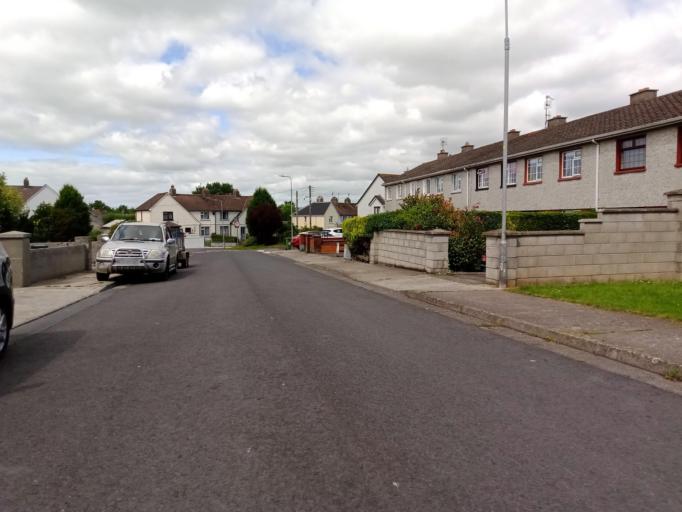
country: IE
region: Leinster
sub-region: Kilkenny
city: Callan
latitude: 52.5417
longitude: -7.3882
